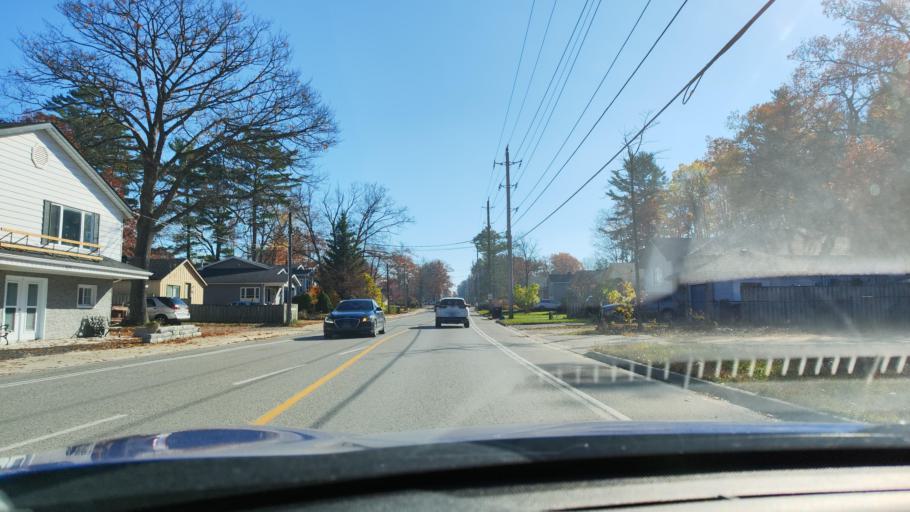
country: CA
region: Ontario
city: Wasaga Beach
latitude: 44.5245
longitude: -80.0003
